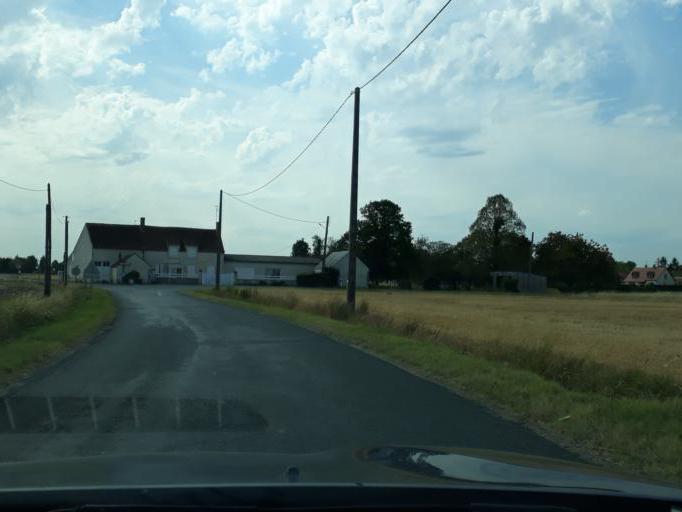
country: FR
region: Centre
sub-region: Departement du Loiret
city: Jargeau
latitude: 47.8478
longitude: 2.1563
